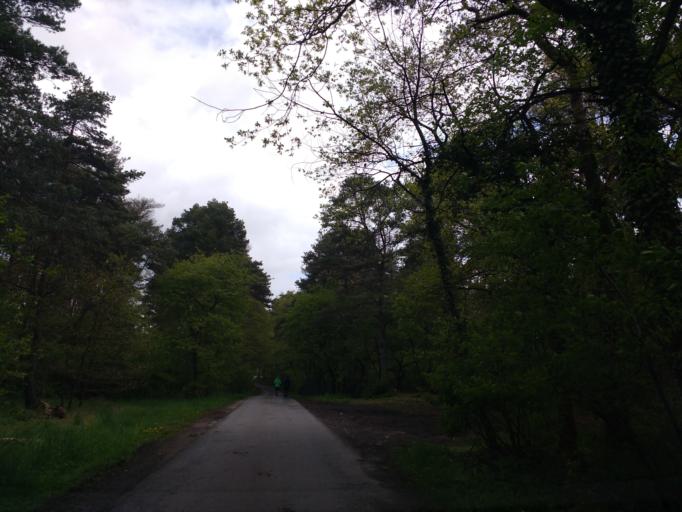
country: DE
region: North Rhine-Westphalia
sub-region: Regierungsbezirk Detmold
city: Augustdorf
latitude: 51.9099
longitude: 8.6843
